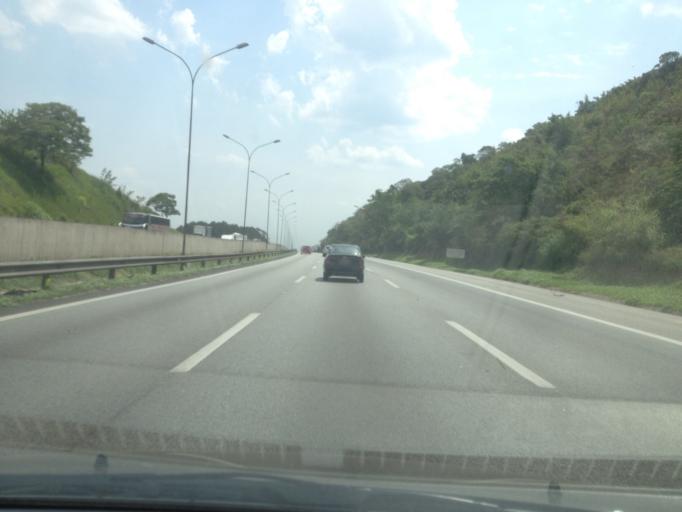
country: BR
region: Sao Paulo
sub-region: Jandira
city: Jandira
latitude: -23.5067
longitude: -46.8994
